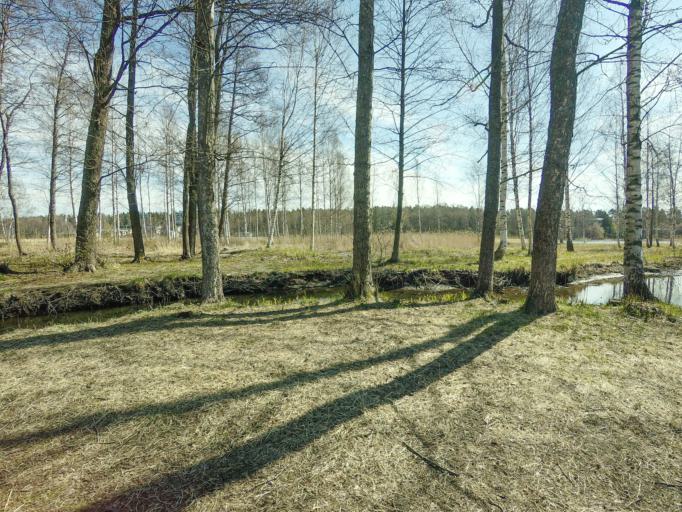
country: FI
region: Uusimaa
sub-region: Helsinki
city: Vantaa
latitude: 60.2177
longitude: 25.1190
